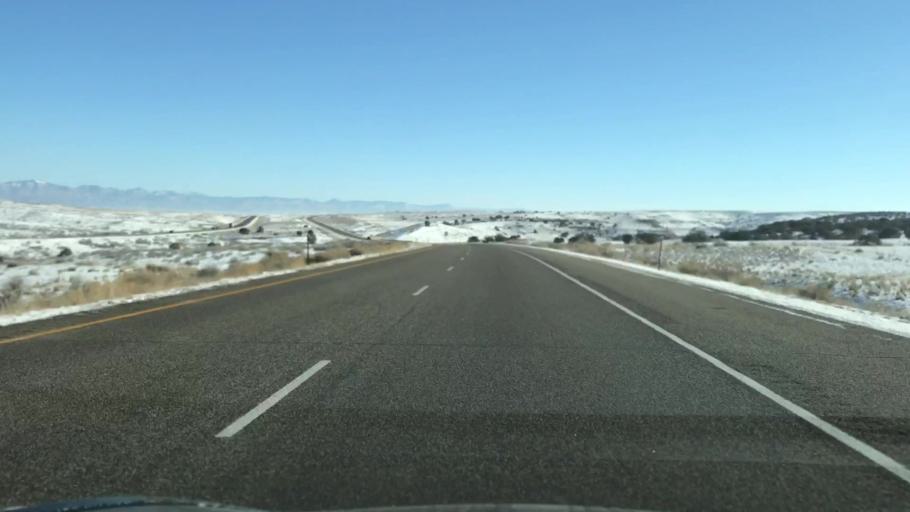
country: US
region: Colorado
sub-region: Mesa County
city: Loma
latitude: 39.2212
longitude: -108.9495
